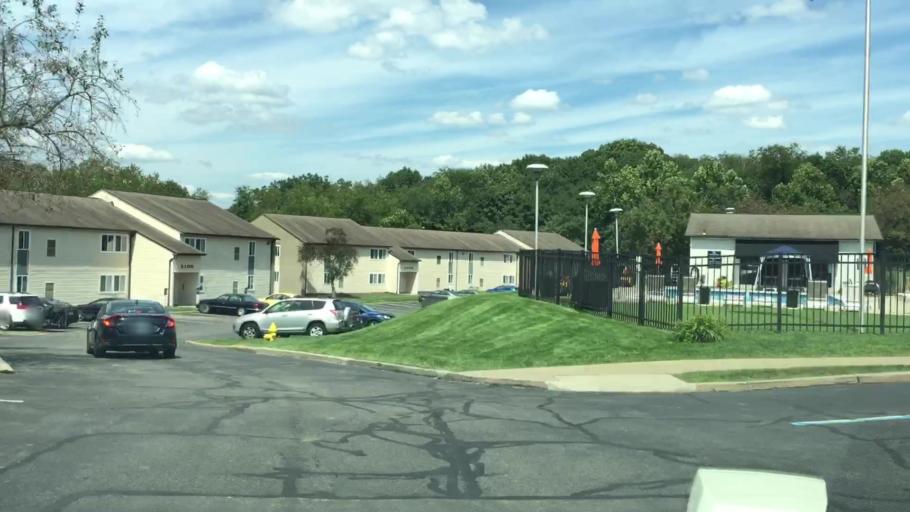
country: US
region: Pennsylvania
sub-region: Allegheny County
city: South Park Township
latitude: 40.2943
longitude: -79.9907
